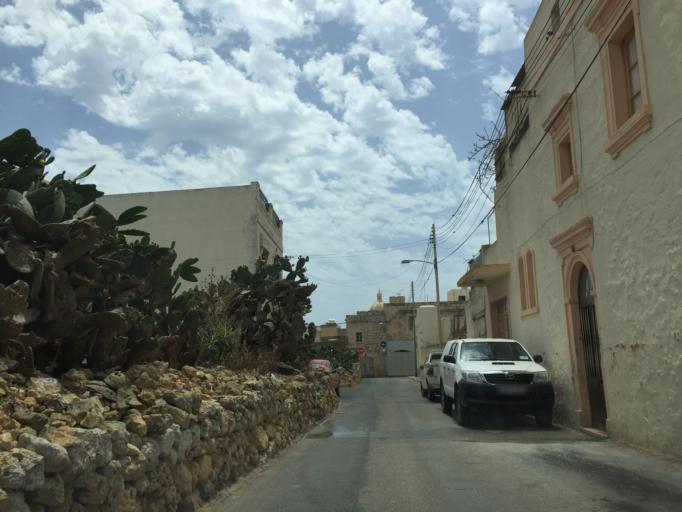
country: MT
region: Iz-Zebbug
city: Zebbug
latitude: 36.0726
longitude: 14.2366
